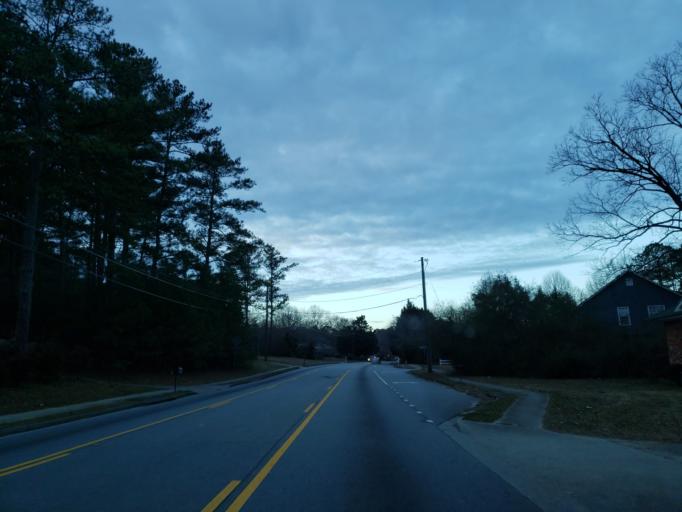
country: US
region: Georgia
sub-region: Cobb County
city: Mableton
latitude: 33.8494
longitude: -84.5869
